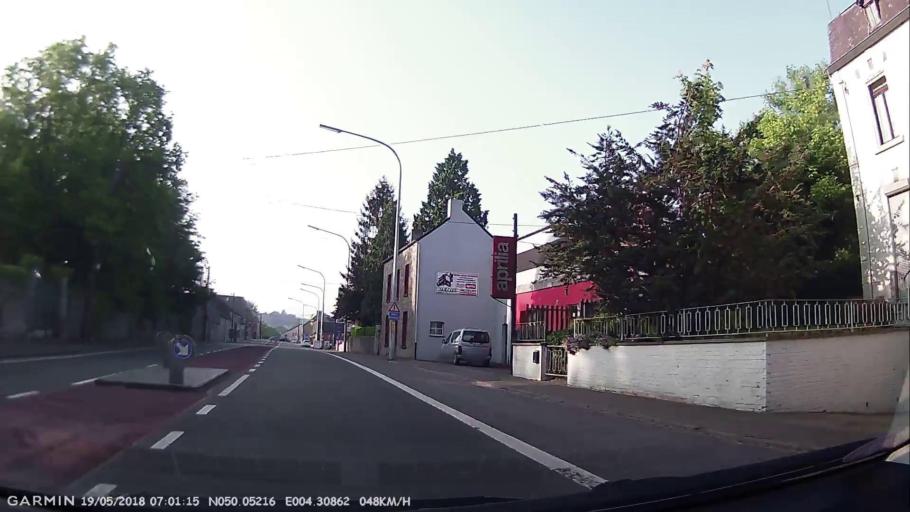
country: BE
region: Wallonia
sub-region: Province du Hainaut
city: Chimay
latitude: 50.0520
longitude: 4.3087
